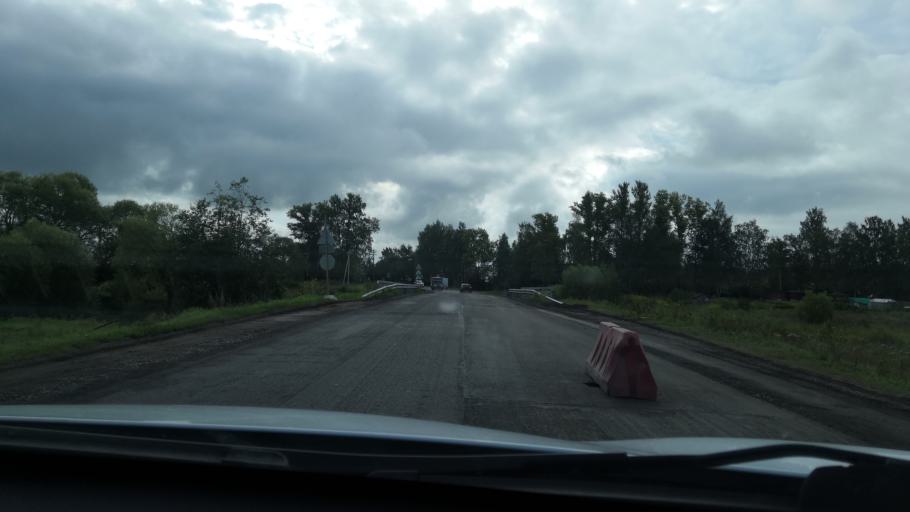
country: RU
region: St.-Petersburg
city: Tyarlevo
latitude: 59.7115
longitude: 30.4675
